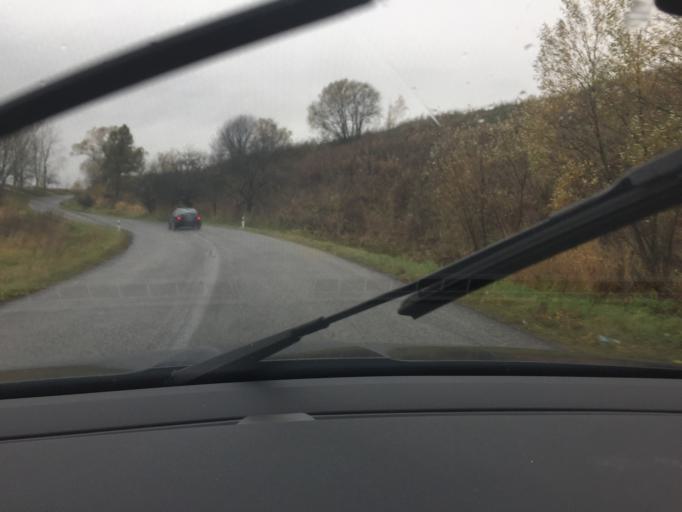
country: SK
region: Presovsky
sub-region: Okres Presov
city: Kezmarok
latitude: 49.1678
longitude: 20.4129
